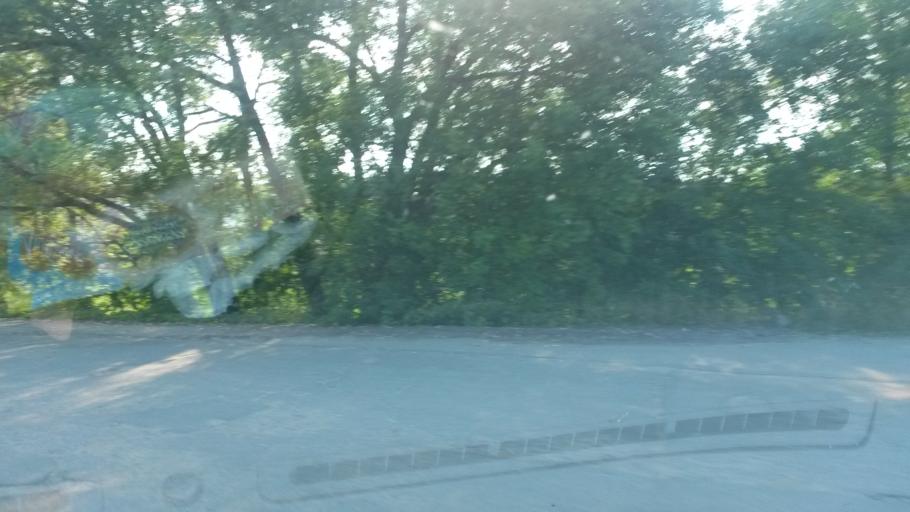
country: RU
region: Jaroslavl
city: Petrovsk
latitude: 57.0040
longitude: 39.2729
